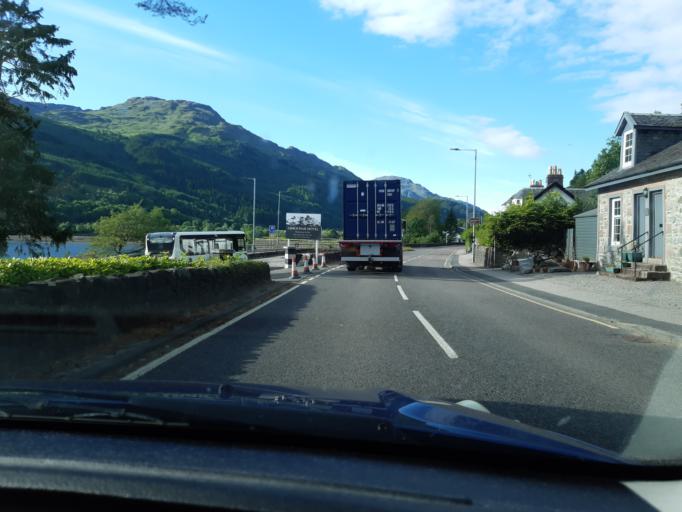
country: GB
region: Scotland
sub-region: Argyll and Bute
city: Garelochhead
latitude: 56.2001
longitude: -4.7456
